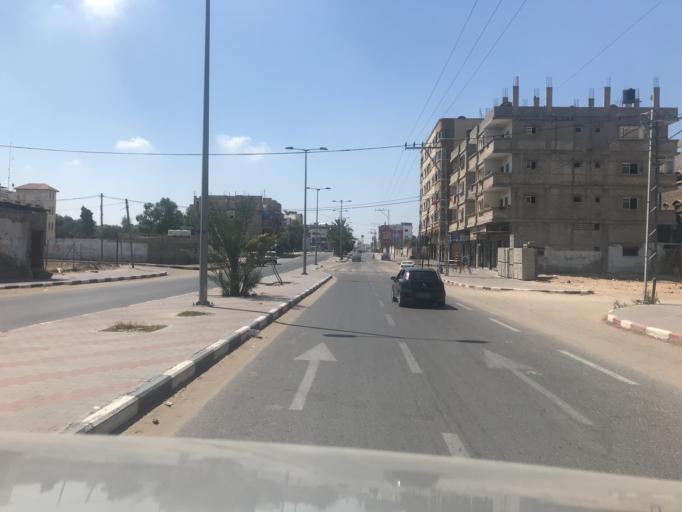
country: PS
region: Gaza Strip
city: Bayt Lahya
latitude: 31.5470
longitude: 34.4745
